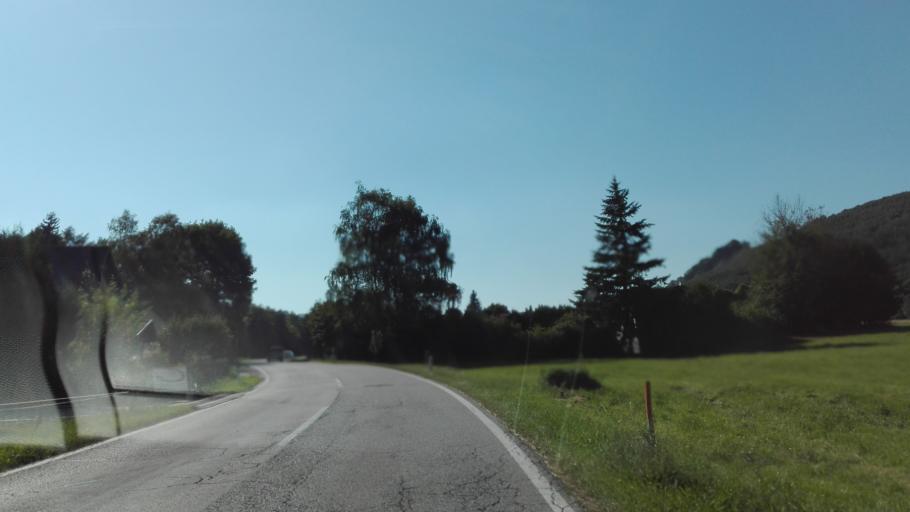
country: AT
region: Lower Austria
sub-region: Politischer Bezirk Baden
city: Klausen-Leopoldsdorf
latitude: 48.0829
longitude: 16.0270
